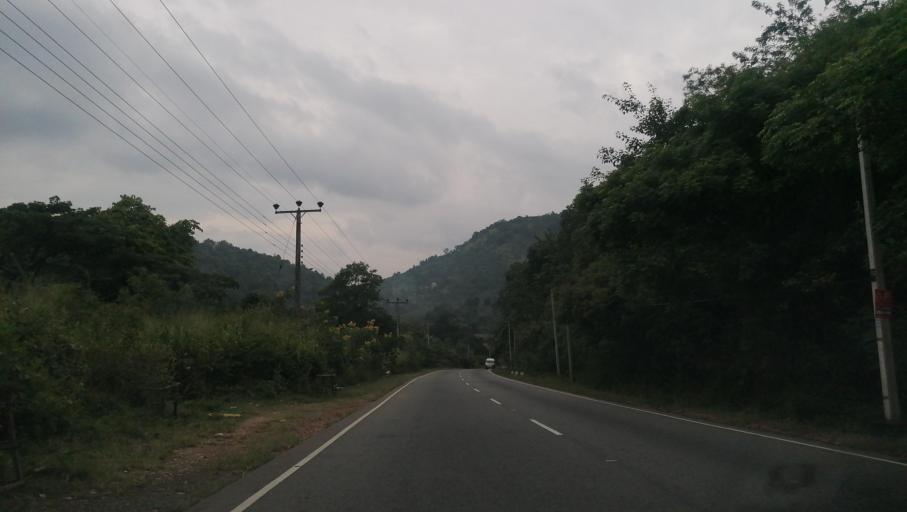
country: LK
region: Central
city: Kandy
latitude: 7.2458
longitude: 80.7277
